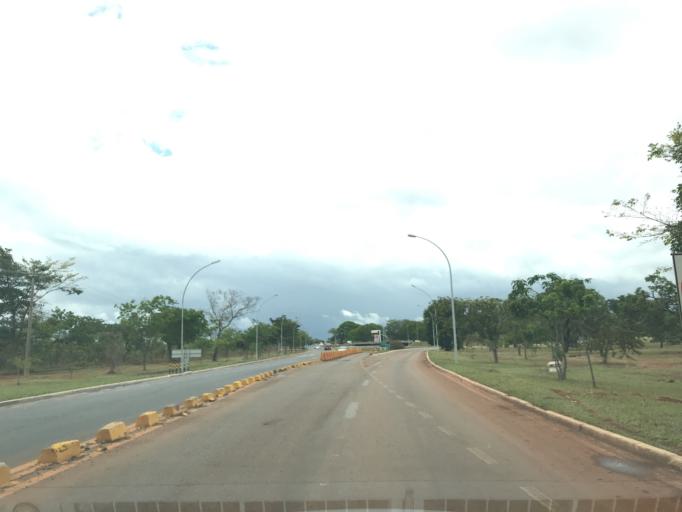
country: BR
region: Federal District
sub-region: Brasilia
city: Brasilia
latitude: -15.8009
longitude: -47.8473
